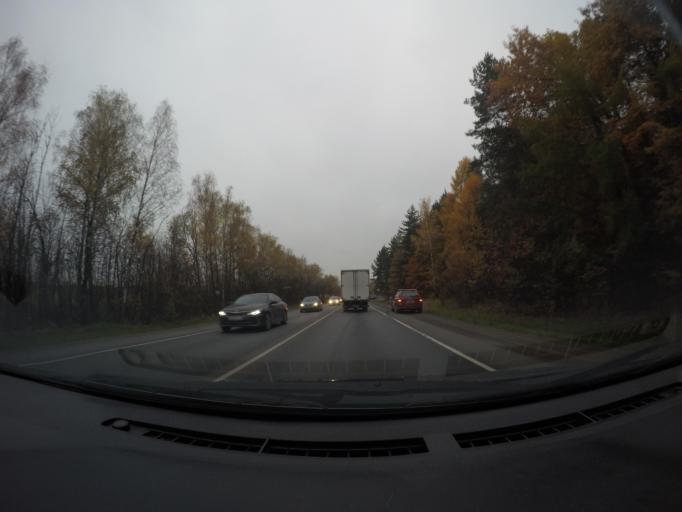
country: RU
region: Moskovskaya
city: Bronnitsy
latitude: 55.4005
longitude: 38.2267
